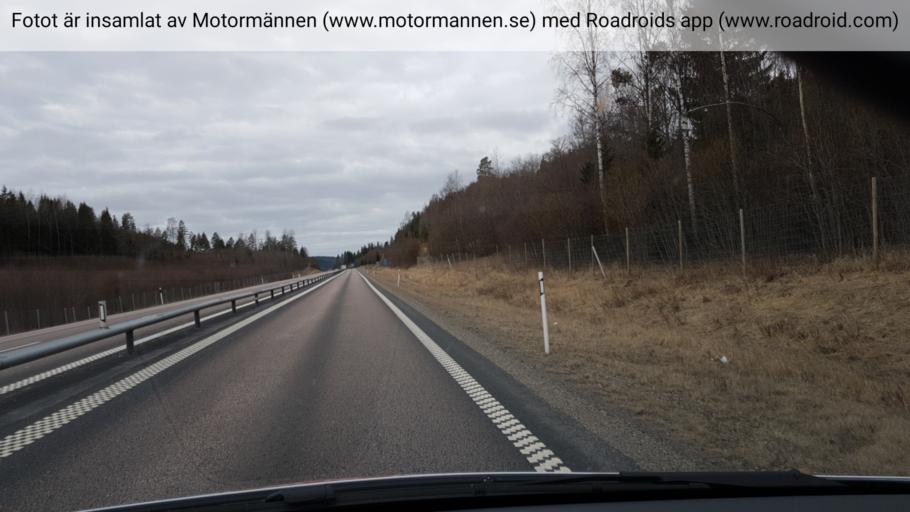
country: SE
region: Vaesternorrland
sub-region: OErnskoeldsviks Kommun
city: Ornskoldsvik
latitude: 63.3123
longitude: 18.8217
